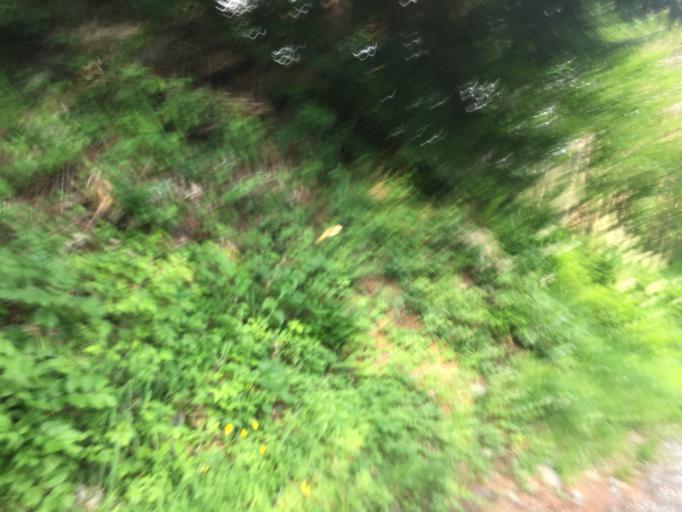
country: FR
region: Rhone-Alpes
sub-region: Departement de la Haute-Savoie
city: Les Houches
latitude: 45.8865
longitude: 6.8088
